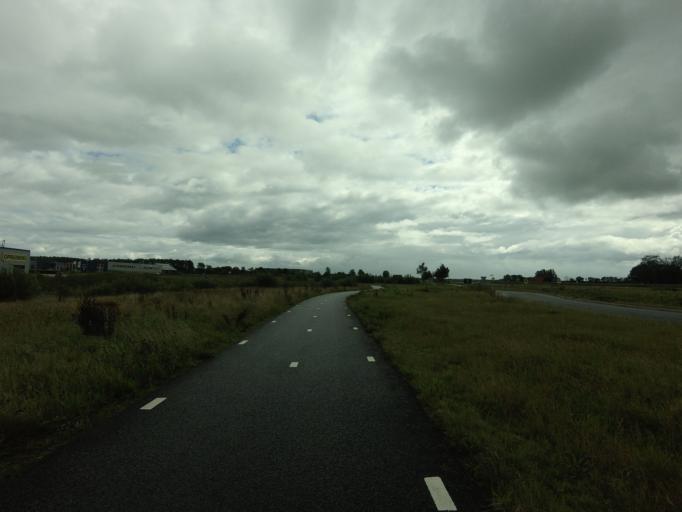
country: NL
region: Drenthe
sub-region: Gemeente Westerveld
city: Dwingeloo
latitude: 52.9776
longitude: 6.2941
